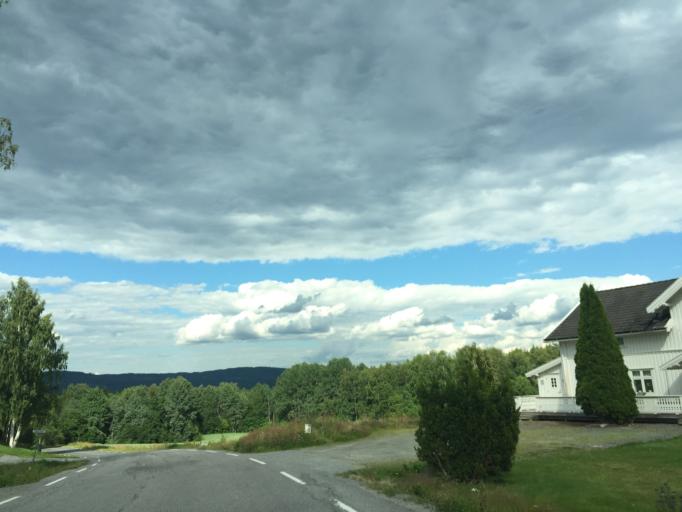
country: NO
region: Hedmark
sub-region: Kongsvinger
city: Spetalen
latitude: 60.1977
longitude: 11.8383
